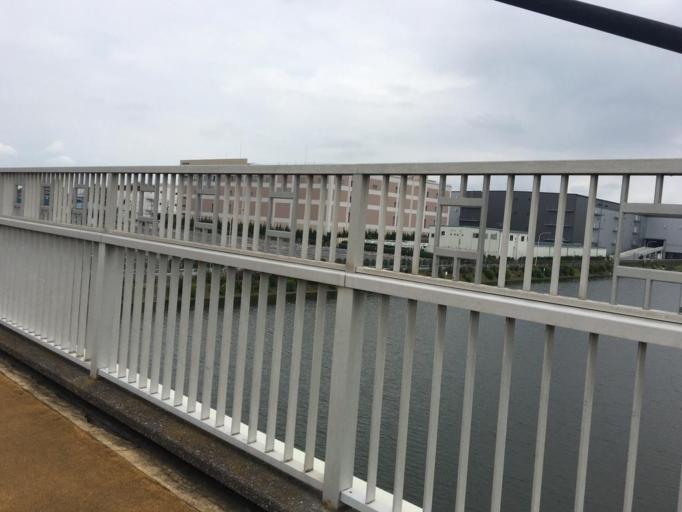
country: JP
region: Saitama
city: Shimotoda
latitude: 35.8036
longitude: 139.6606
